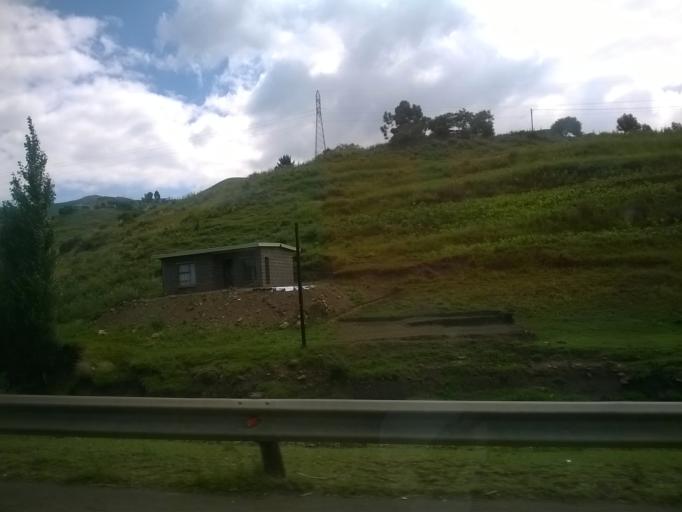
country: LS
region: Butha-Buthe
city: Butha-Buthe
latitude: -29.1130
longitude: 28.4908
